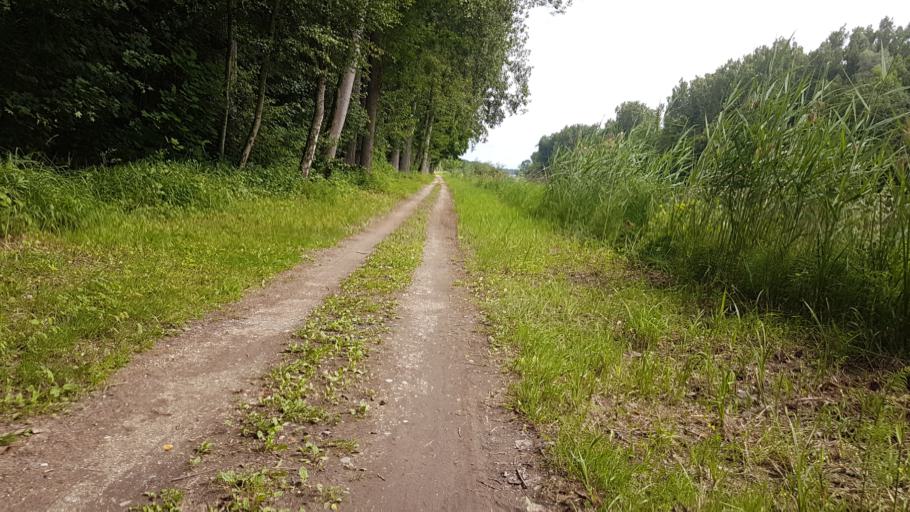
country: DE
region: Bavaria
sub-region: Swabia
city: Gundremmingen
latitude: 48.5240
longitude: 10.3872
